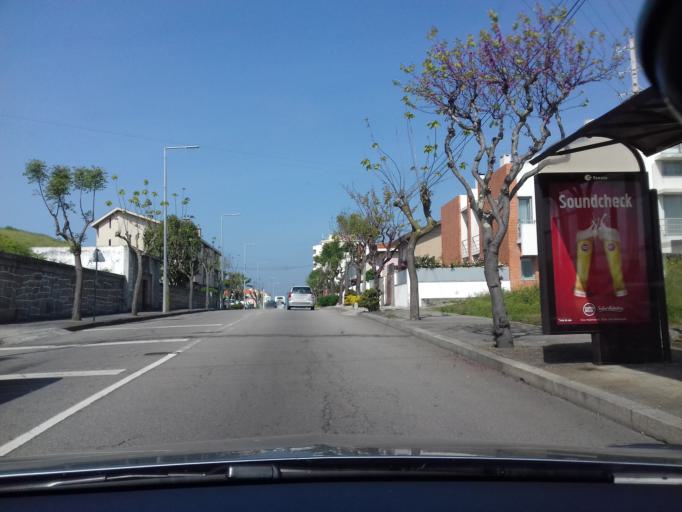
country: PT
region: Aveiro
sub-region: Espinho
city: Silvalde
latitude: 41.0084
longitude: -8.6254
